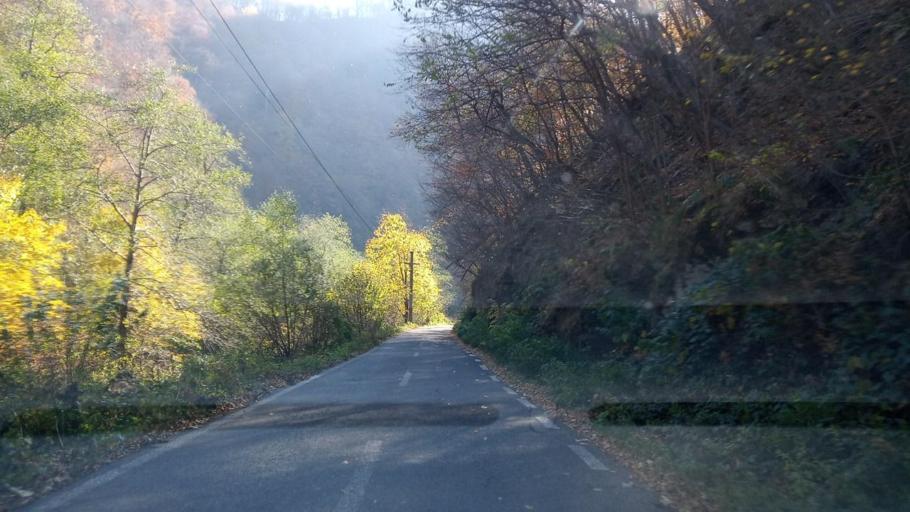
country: RO
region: Sibiu
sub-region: Comuna Boita
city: Boita
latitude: 45.5601
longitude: 24.2605
